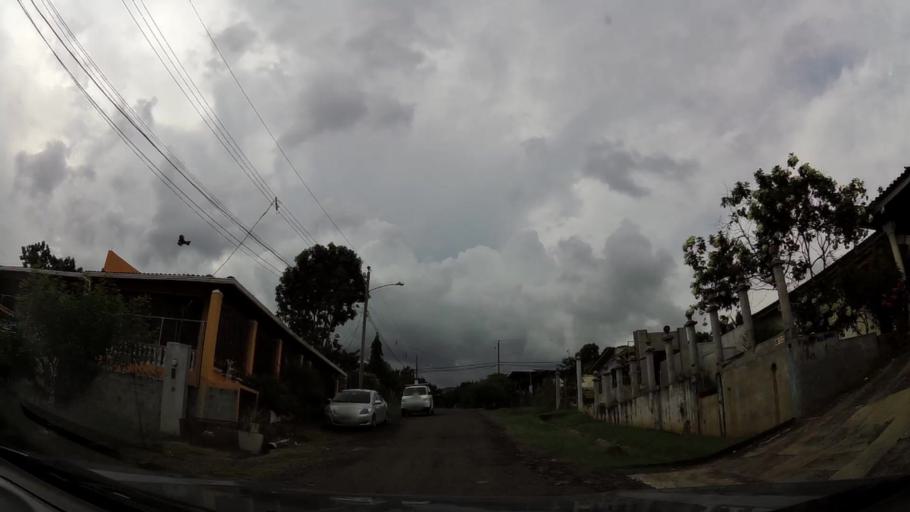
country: PA
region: Panama
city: Tocumen
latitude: 9.1115
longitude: -79.3797
